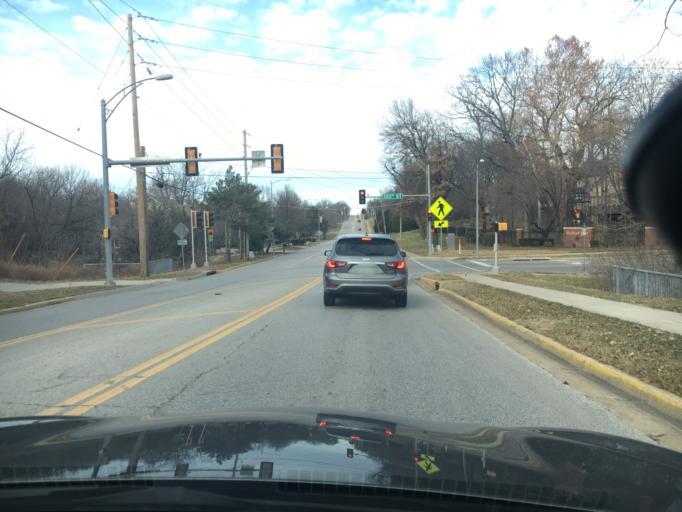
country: US
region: Kansas
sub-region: Johnson County
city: Leawood
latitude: 38.9052
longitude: -94.6305
